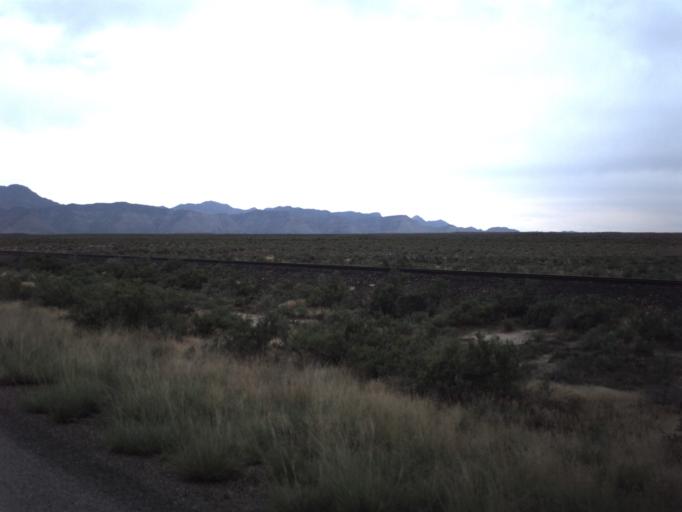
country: US
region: Utah
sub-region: Carbon County
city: East Carbon City
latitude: 39.5330
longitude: -110.5347
